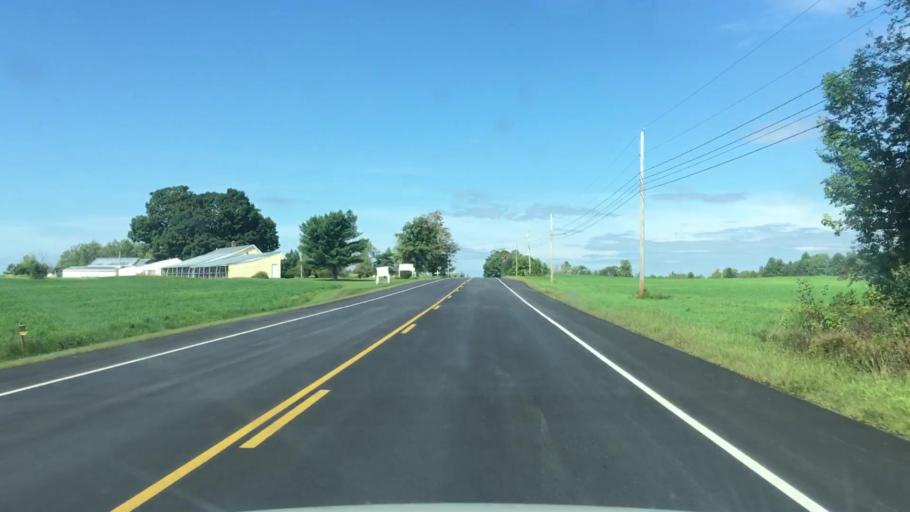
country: US
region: Maine
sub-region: Penobscot County
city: Corinna
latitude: 44.9523
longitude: -69.2545
